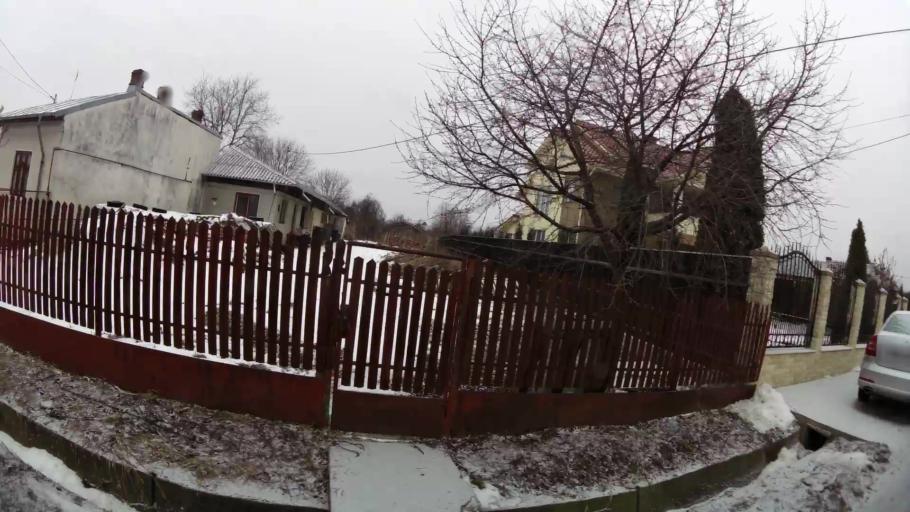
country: RO
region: Dambovita
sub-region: Municipiul Targoviste
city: Targoviste
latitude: 44.9406
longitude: 25.4752
